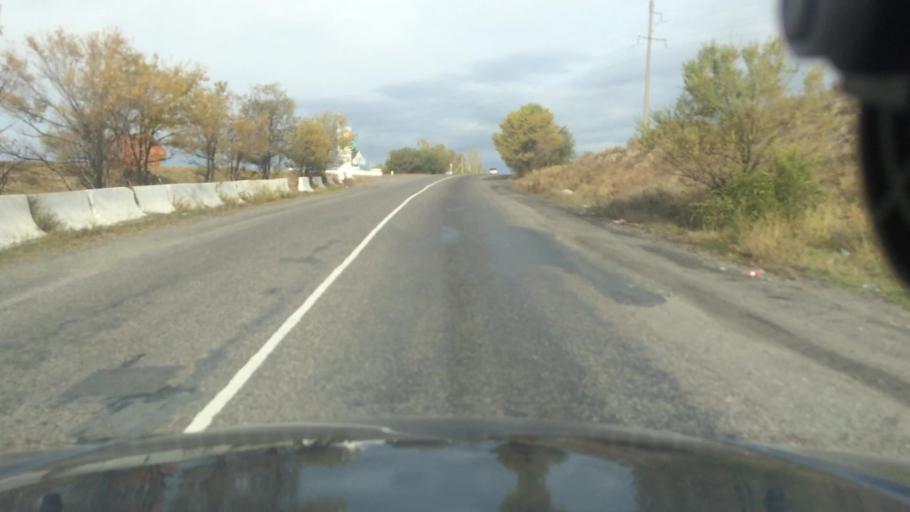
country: KG
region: Ysyk-Koel
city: Karakol
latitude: 42.5977
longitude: 78.3758
